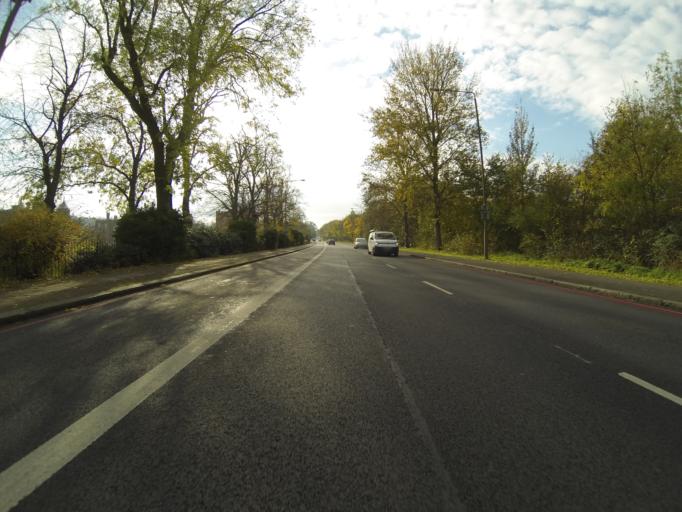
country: GB
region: England
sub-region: Greater London
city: Woolwich
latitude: 51.4773
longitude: 0.0577
